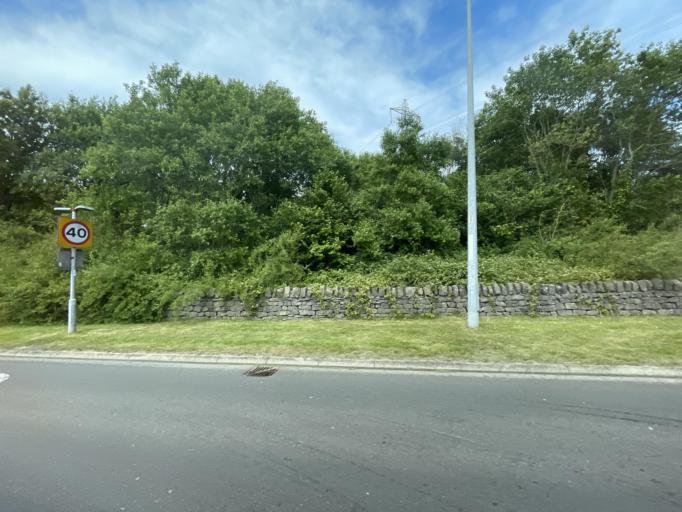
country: GB
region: Wales
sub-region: Anglesey
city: Llanfairpwllgwyngyll
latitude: 53.2220
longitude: -4.2178
